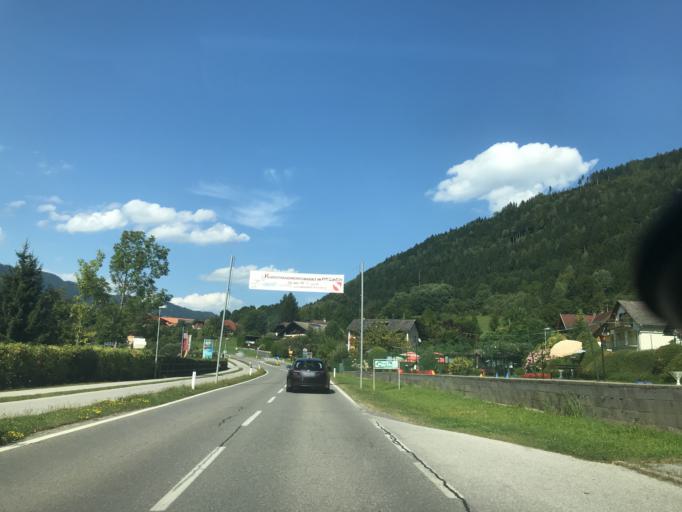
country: AT
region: Carinthia
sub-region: Politischer Bezirk Feldkirchen
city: Ossiach
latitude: 46.6643
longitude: 13.9762
